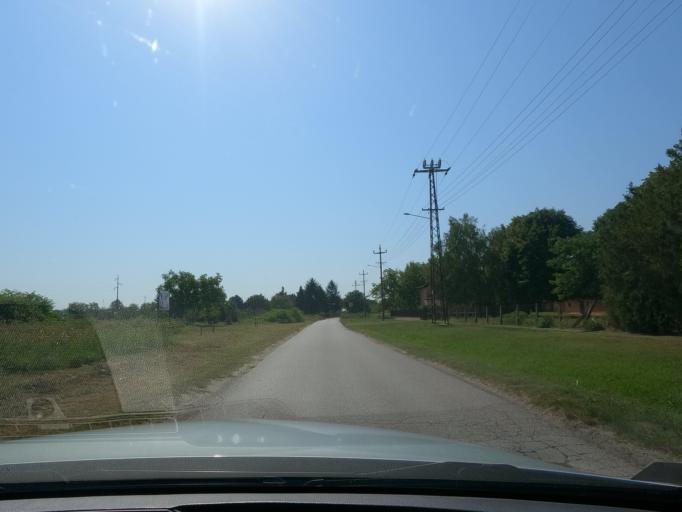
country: HU
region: Csongrad
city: Asotthalom
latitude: 46.0999
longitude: 19.7777
